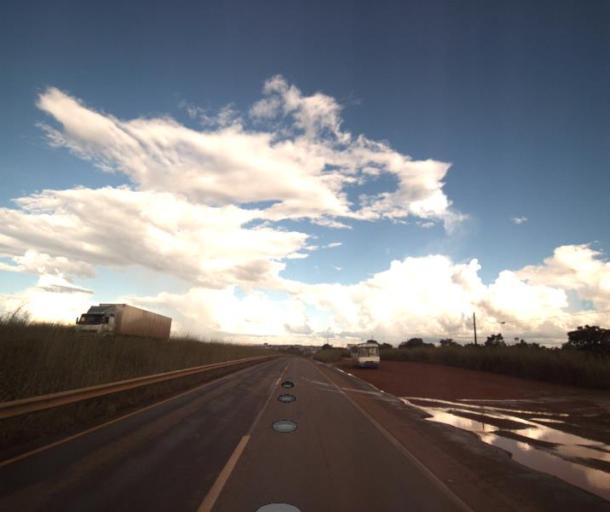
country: BR
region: Goias
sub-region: Anapolis
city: Anapolis
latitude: -16.2577
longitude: -48.9890
